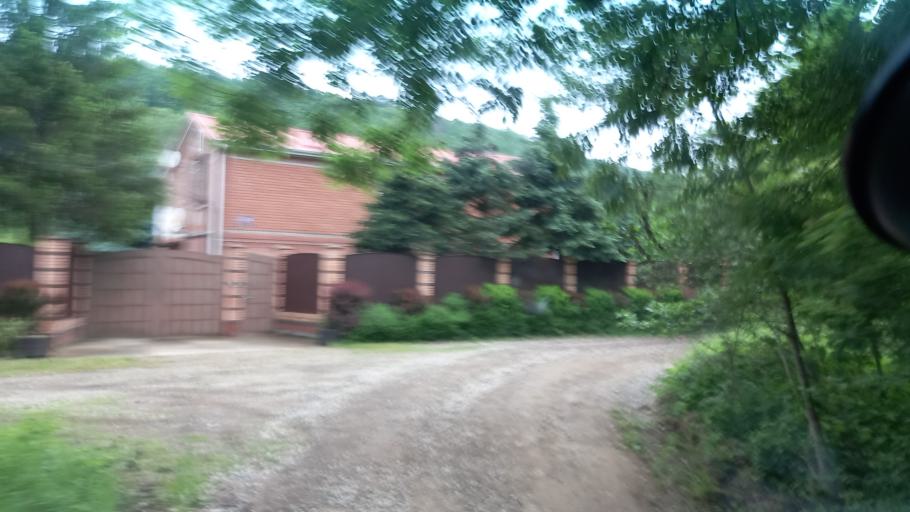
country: RU
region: Krasnodarskiy
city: Azovskaya
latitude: 44.6342
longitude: 38.6125
